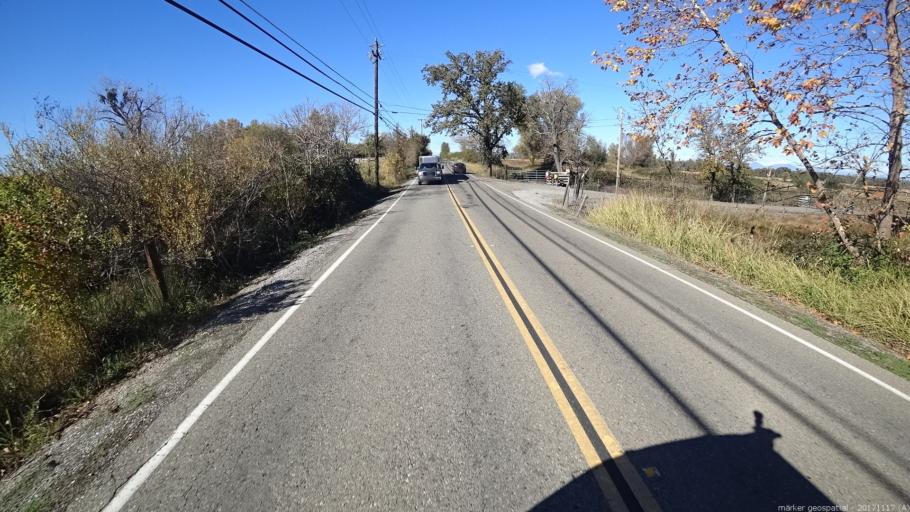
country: US
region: California
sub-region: Shasta County
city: Cottonwood
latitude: 40.4296
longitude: -122.2300
